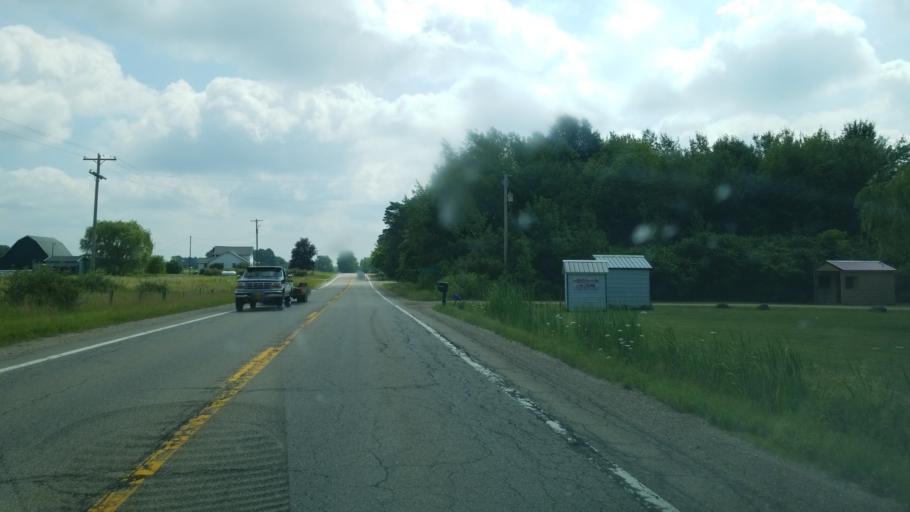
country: US
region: Michigan
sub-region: Kent County
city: Kent City
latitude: 43.2197
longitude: -85.7047
